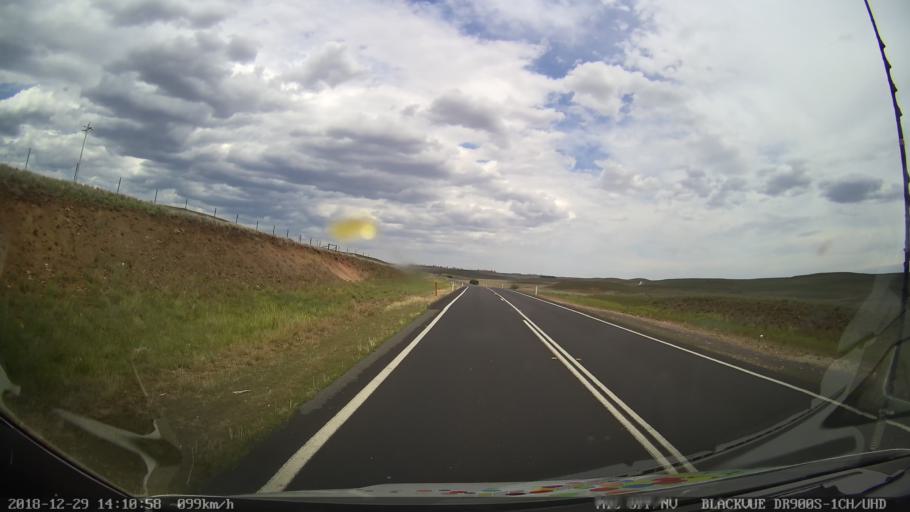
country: AU
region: New South Wales
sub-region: Cooma-Monaro
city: Cooma
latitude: -36.3992
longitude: 149.2172
